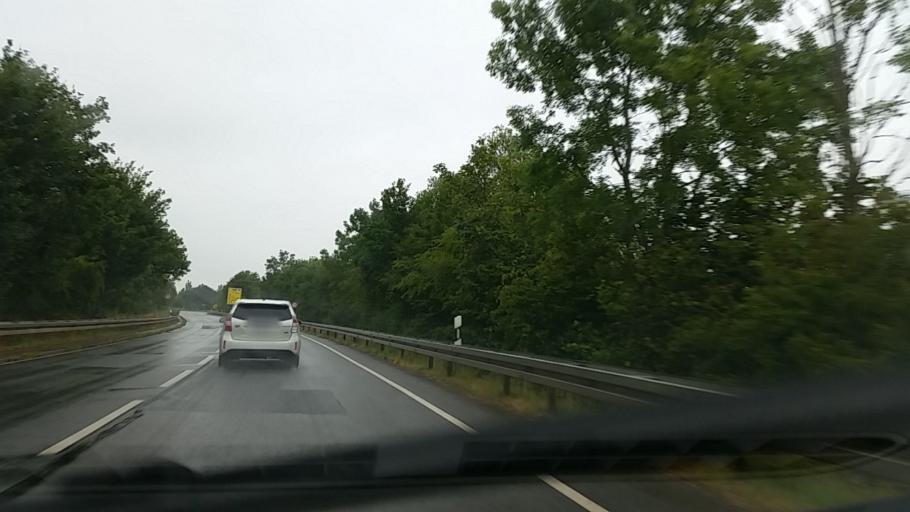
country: DE
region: Mecklenburg-Vorpommern
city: Kropelin
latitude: 54.0732
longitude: 11.7860
